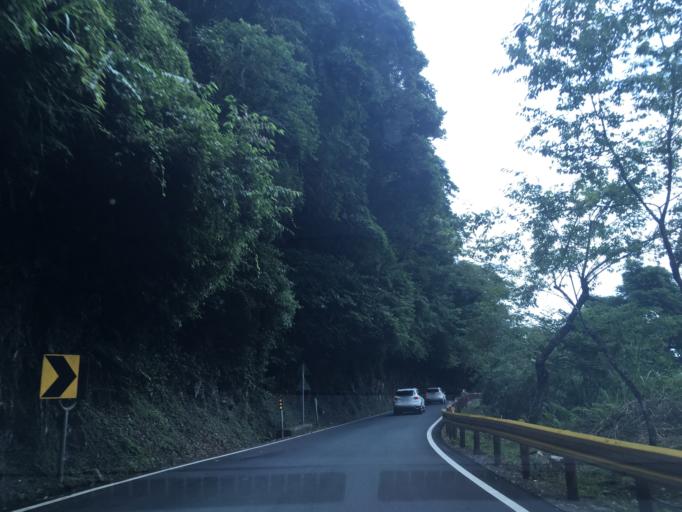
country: TW
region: Taiwan
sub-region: Hualien
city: Hualian
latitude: 24.1948
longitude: 121.4169
